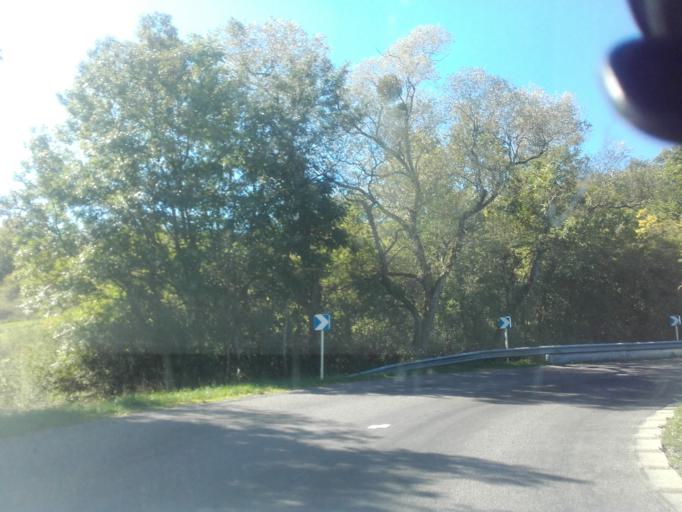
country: FR
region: Bourgogne
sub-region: Departement de la Cote-d'Or
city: Meursault
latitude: 47.0069
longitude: 4.7089
